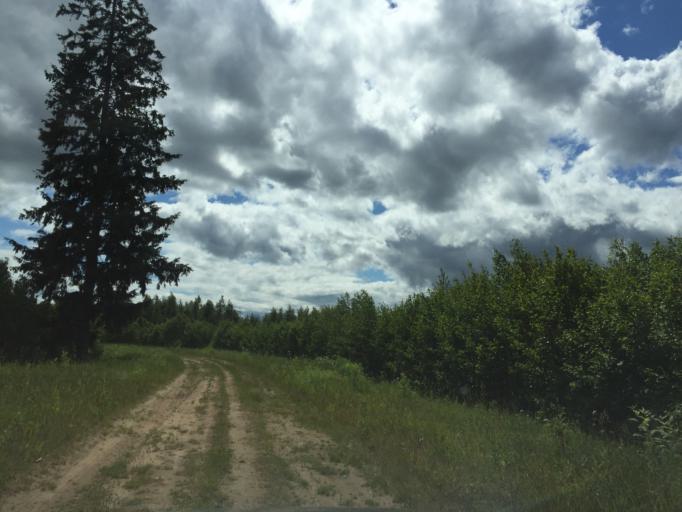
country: LV
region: Lecava
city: Iecava
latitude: 56.5564
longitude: 24.3417
